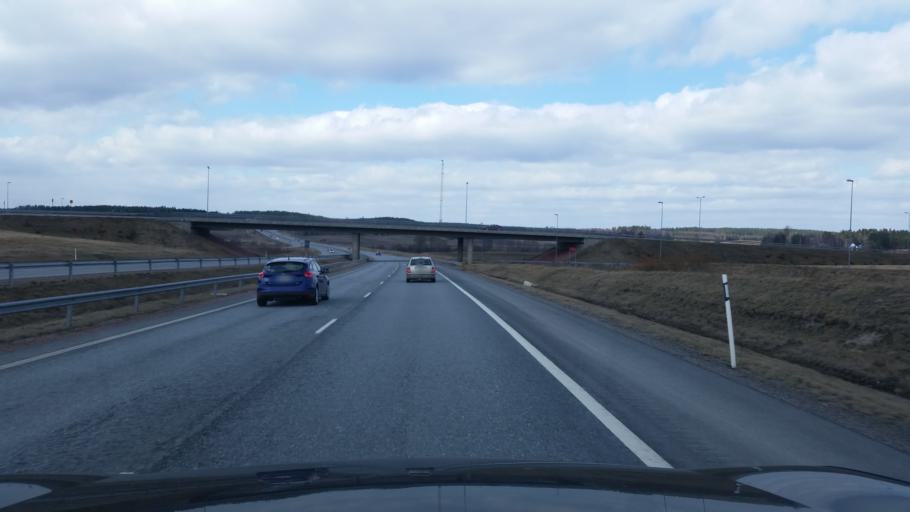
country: FI
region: Varsinais-Suomi
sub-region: Salo
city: Suomusjaervi
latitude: 60.3888
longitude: 23.5878
